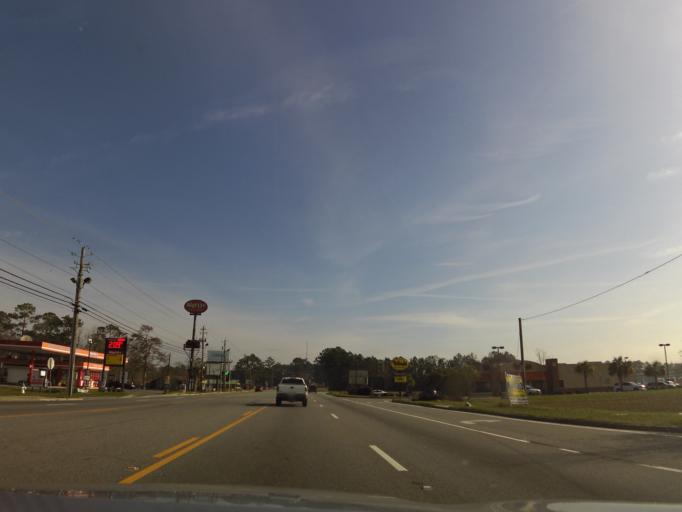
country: US
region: Georgia
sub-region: Lowndes County
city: Remerton
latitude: 30.8212
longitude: -83.3105
